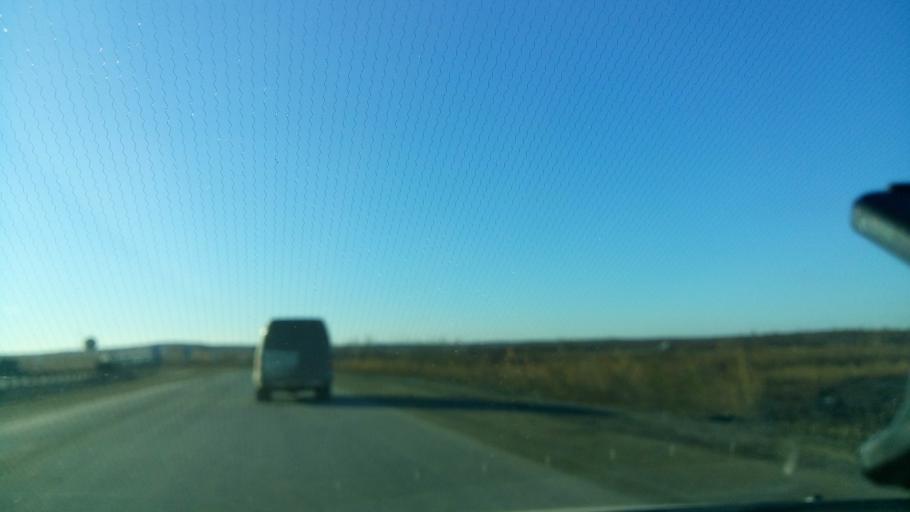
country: RU
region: Sverdlovsk
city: Sovkhoznyy
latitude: 56.7341
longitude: 60.5425
